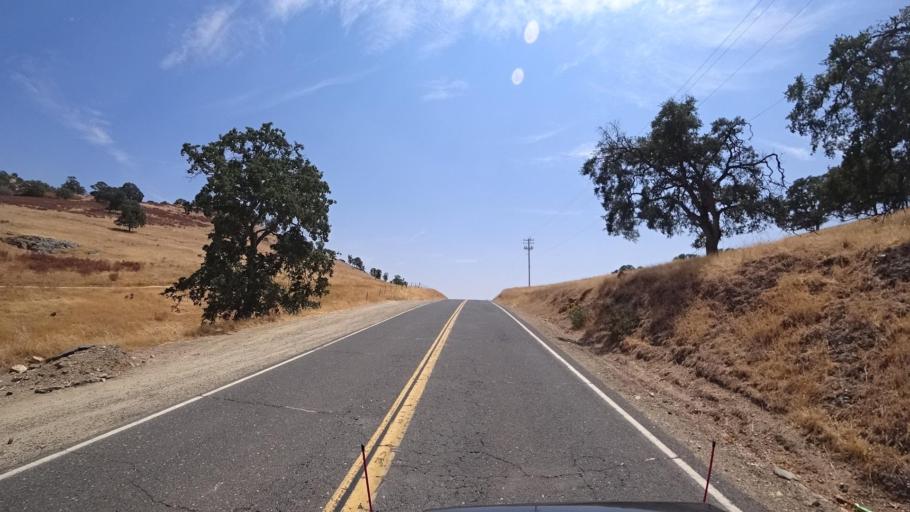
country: US
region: California
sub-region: Merced County
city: Planada
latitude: 37.6281
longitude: -120.3082
